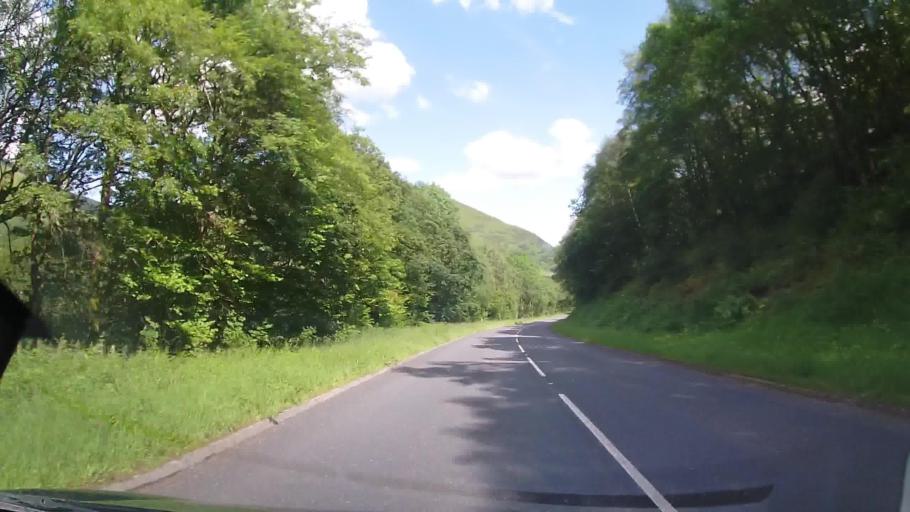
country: GB
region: Wales
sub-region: Gwynedd
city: Corris
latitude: 52.7326
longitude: -3.7230
